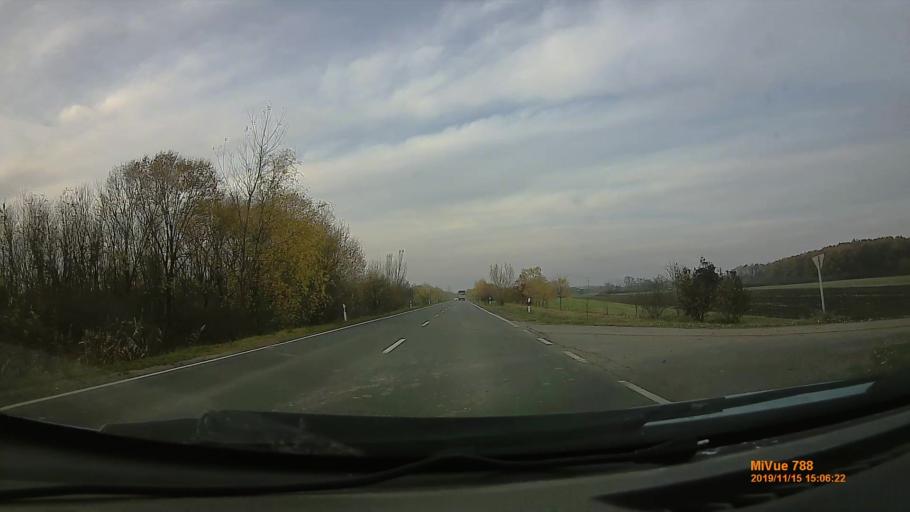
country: HU
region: Bekes
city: Gyula
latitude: 46.6419
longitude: 21.2457
